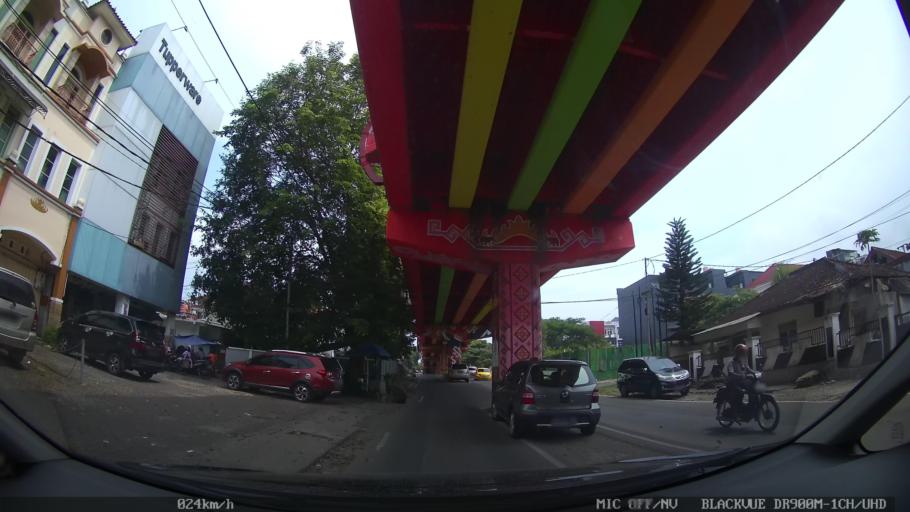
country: ID
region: Lampung
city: Bandarlampung
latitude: -5.4220
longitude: 105.2696
